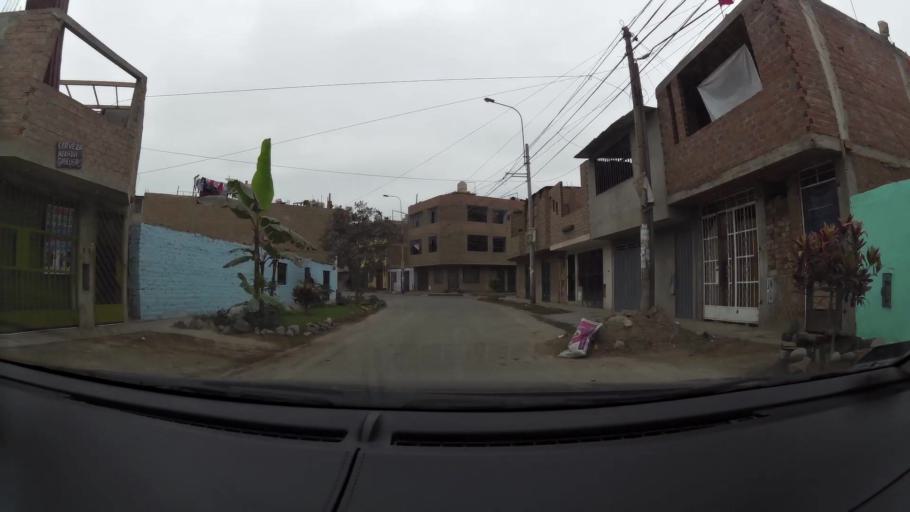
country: PE
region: Lima
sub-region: Lima
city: Independencia
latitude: -11.9519
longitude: -77.0837
